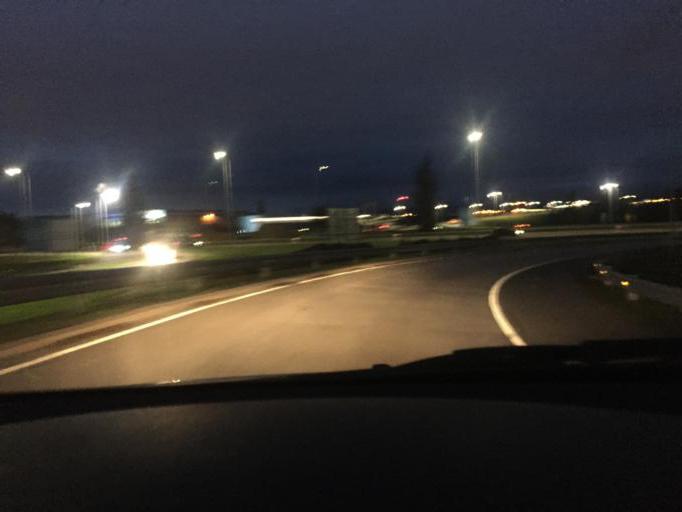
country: AR
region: Cordoba
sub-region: Departamento de Capital
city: Cordoba
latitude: -31.3552
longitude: -64.2018
